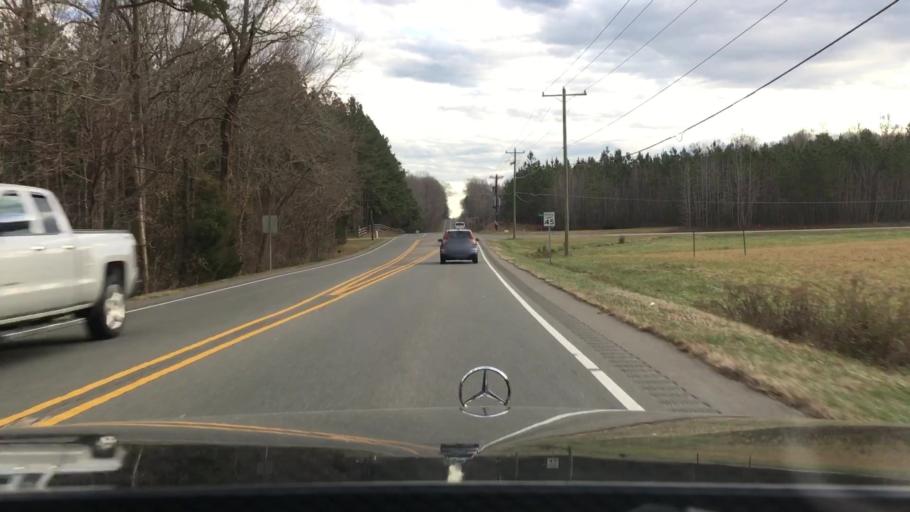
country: US
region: North Carolina
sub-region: Orange County
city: Hillsborough
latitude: 36.1098
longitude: -79.1108
